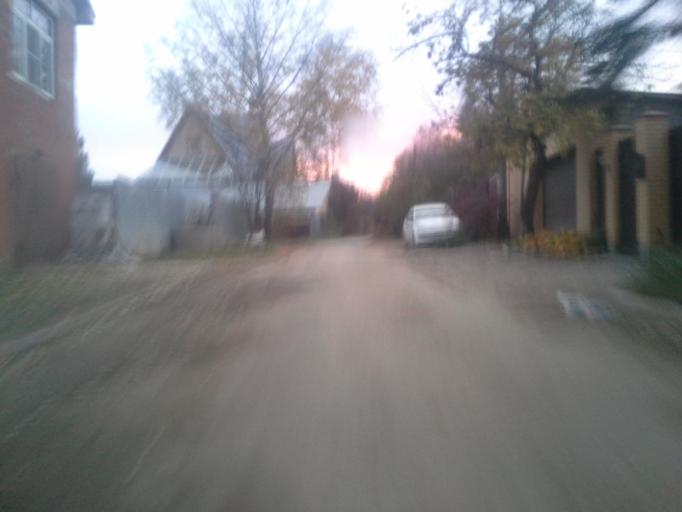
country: RU
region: Moskovskaya
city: Lesnoy Gorodok
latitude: 55.6363
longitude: 37.2323
